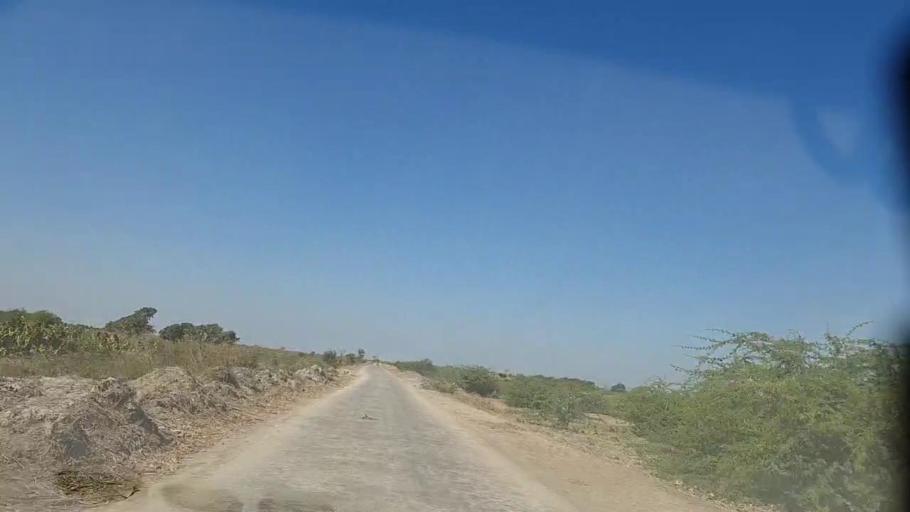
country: PK
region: Sindh
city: Mirwah Gorchani
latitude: 25.2206
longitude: 69.0255
